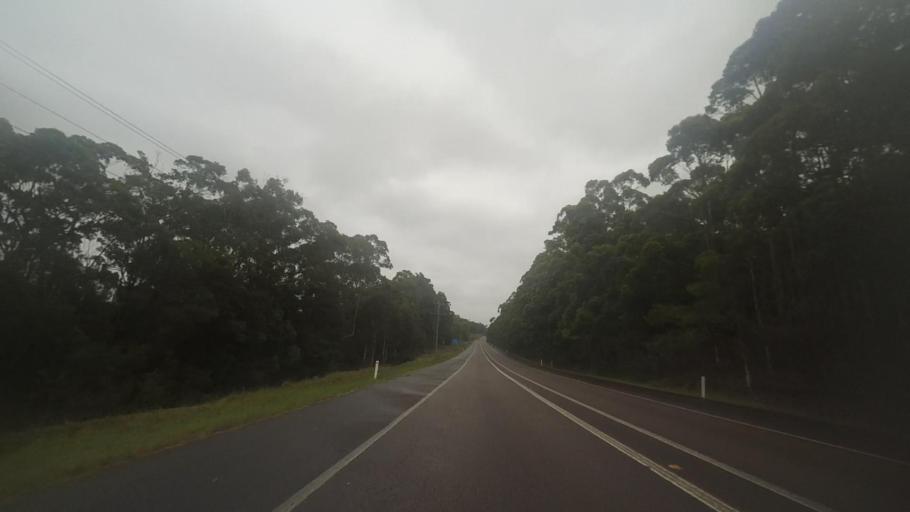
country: AU
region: New South Wales
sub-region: Port Stephens Shire
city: Port Stephens
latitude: -32.6402
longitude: 151.9913
